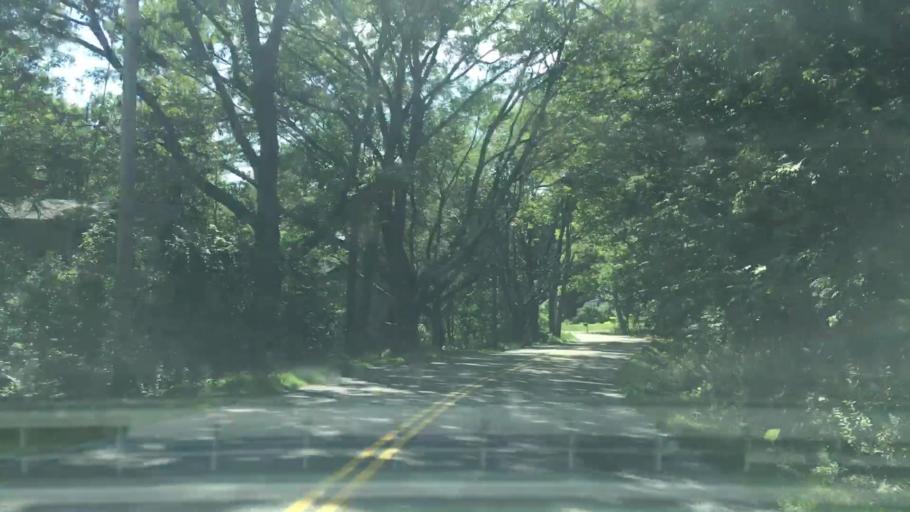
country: US
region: Maine
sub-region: Cumberland County
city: South Portland
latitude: 43.6168
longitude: -70.2585
